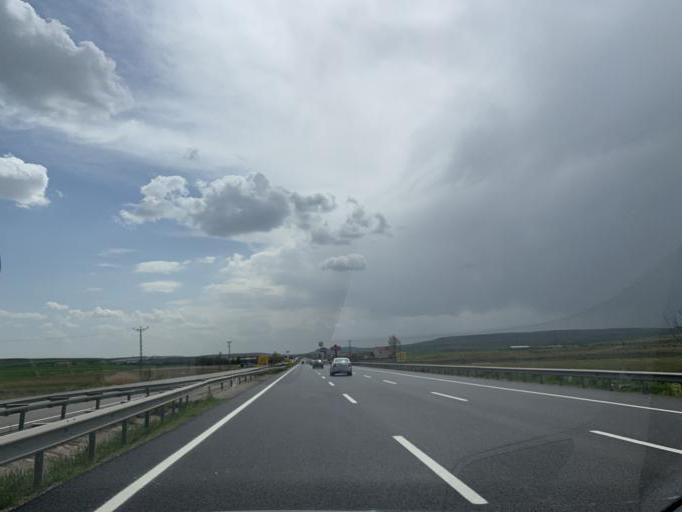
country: TR
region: Ankara
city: Polatli
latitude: 39.6631
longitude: 32.2242
